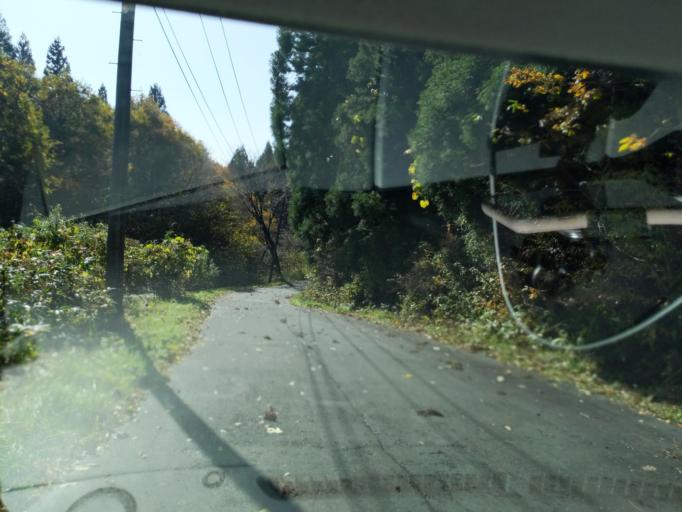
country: JP
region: Iwate
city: Ichinoseki
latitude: 39.0227
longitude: 141.0965
